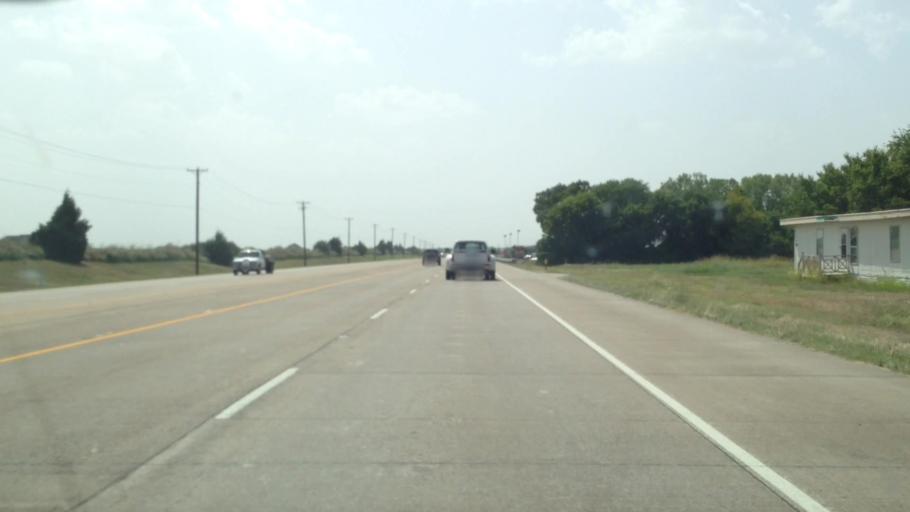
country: US
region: Texas
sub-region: Collin County
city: Princeton
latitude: 33.1665
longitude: -96.4561
